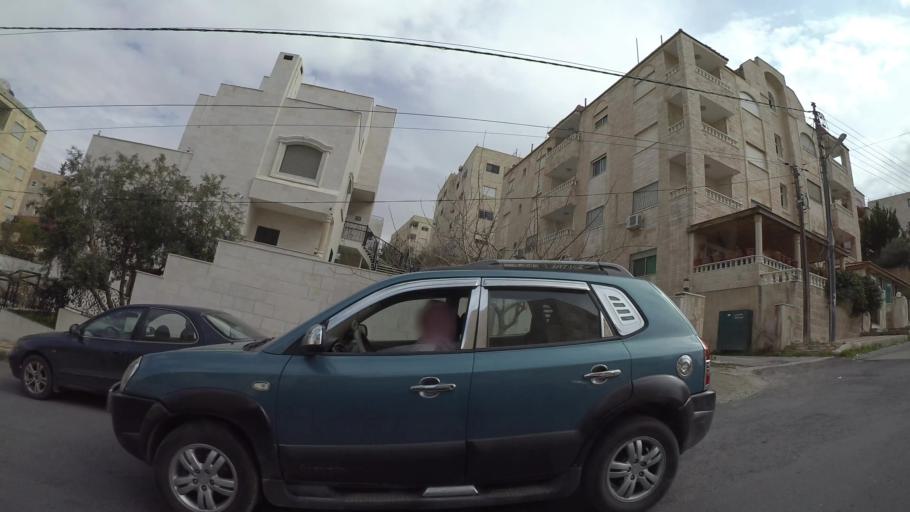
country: JO
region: Amman
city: Amman
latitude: 32.0024
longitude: 35.9381
